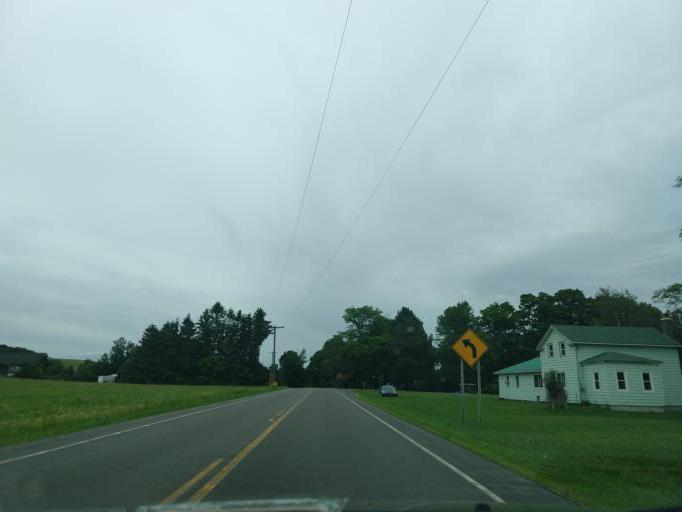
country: US
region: New York
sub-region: Tompkins County
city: Dryden
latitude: 42.4880
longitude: -76.2493
